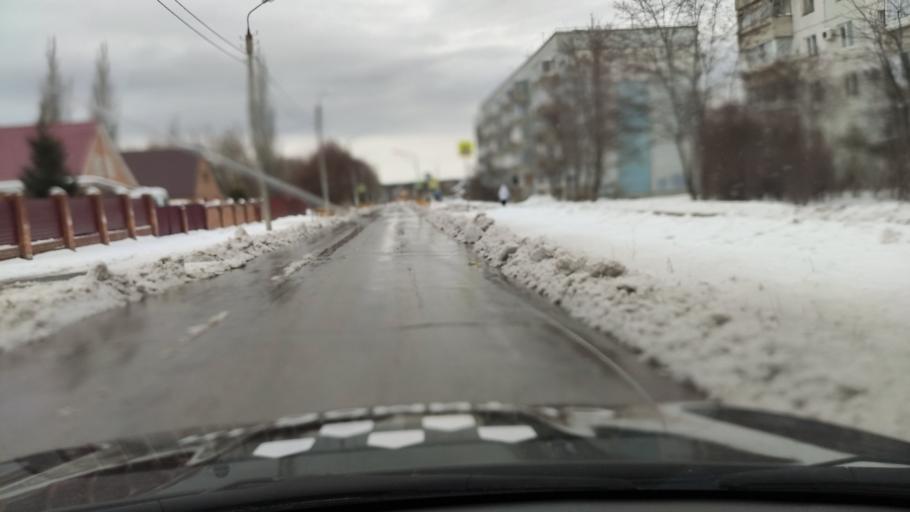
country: RU
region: Samara
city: Povolzhskiy
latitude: 53.5896
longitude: 49.7618
